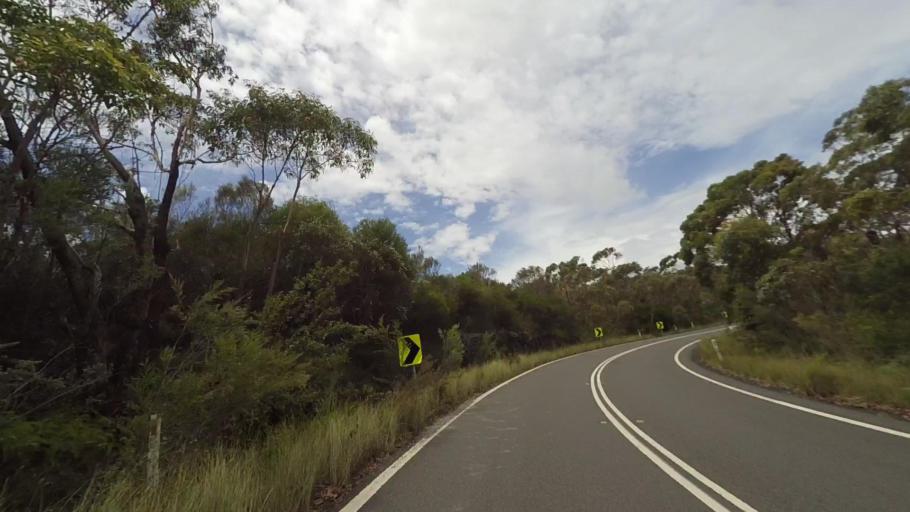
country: AU
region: New South Wales
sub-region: Sutherland Shire
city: Grays Point
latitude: -34.1214
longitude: 151.0784
